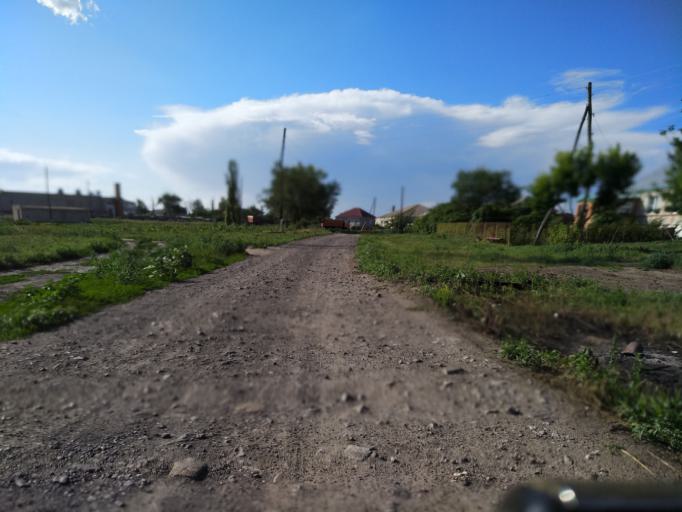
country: RU
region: Lipetsk
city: Dobrinka
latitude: 52.0361
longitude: 40.5579
